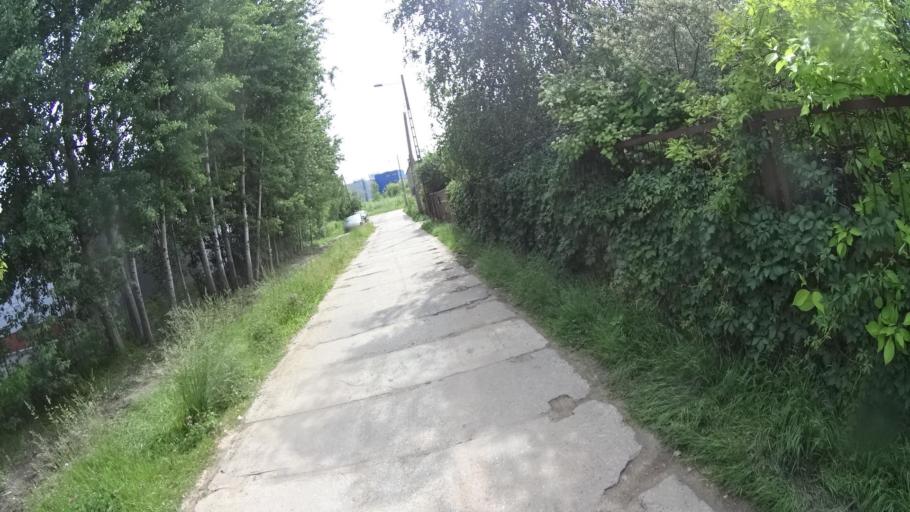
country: PL
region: Masovian Voivodeship
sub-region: Powiat pruszkowski
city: Raszyn
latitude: 52.1708
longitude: 20.9289
